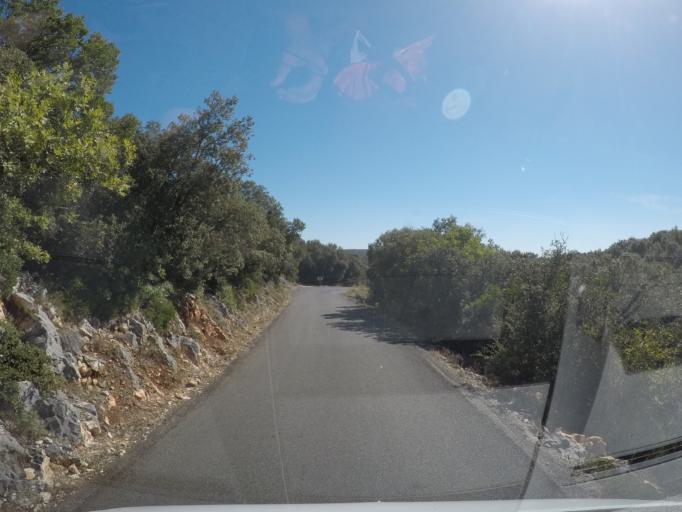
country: FR
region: Languedoc-Roussillon
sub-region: Departement de l'Herault
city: Vailhauques
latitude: 43.7132
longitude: 3.6818
